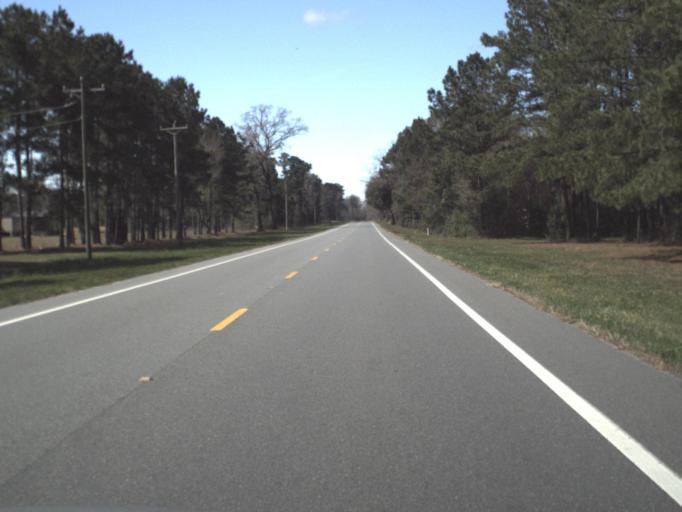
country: US
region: Florida
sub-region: Gadsden County
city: Gretna
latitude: 30.6779
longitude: -84.7071
